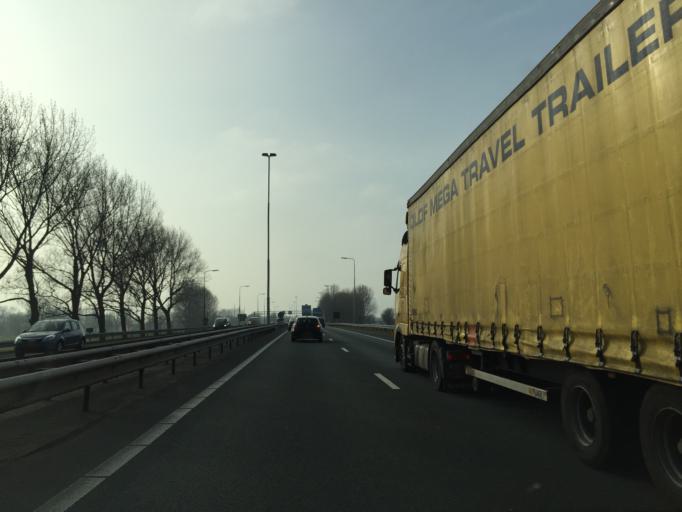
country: NL
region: South Holland
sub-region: Gemeente Maassluis
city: Maassluis
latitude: 51.9228
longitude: 4.2834
